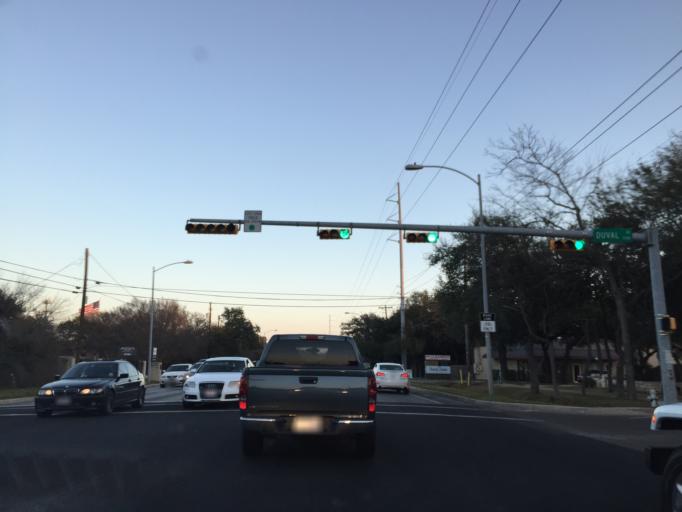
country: US
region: Texas
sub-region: Williamson County
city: Jollyville
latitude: 30.4174
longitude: -97.7501
